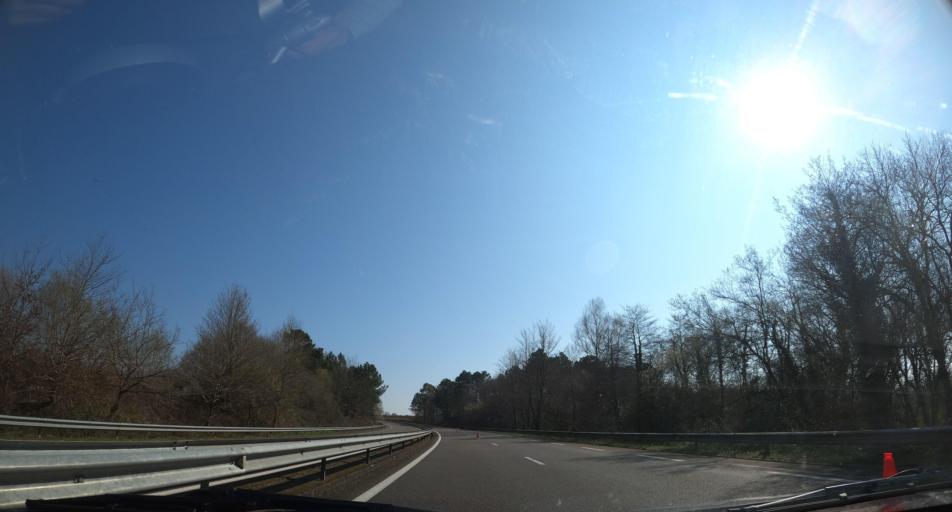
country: FR
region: Aquitaine
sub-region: Departement des Landes
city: Meilhan
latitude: 43.8601
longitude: -0.7024
